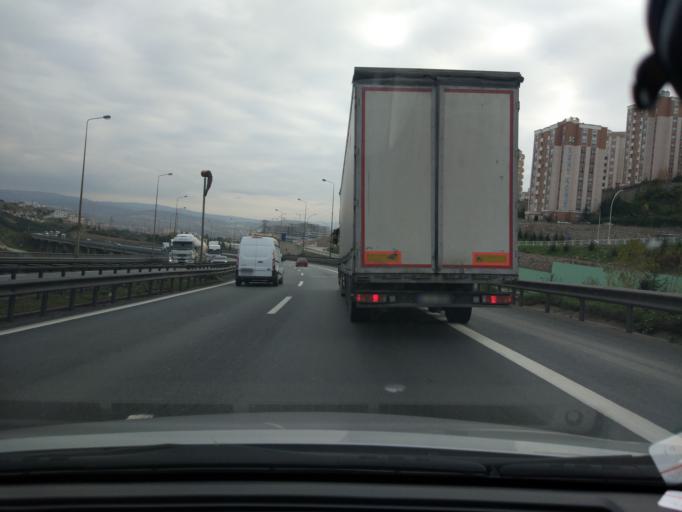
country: TR
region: Kocaeli
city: Izmit
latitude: 40.7823
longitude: 29.9393
